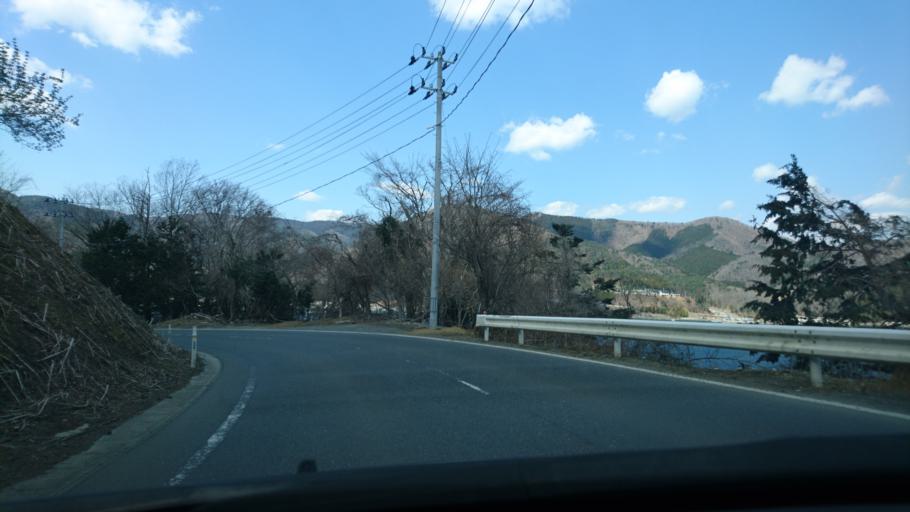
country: JP
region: Miyagi
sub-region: Oshika Gun
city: Onagawa Cho
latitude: 38.4620
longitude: 141.4821
